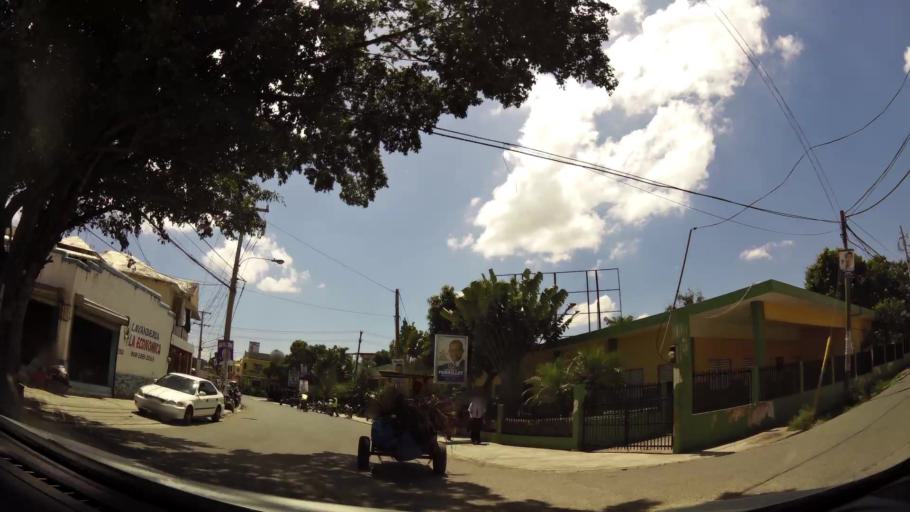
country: DO
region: San Cristobal
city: San Cristobal
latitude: 18.4048
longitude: -70.1070
